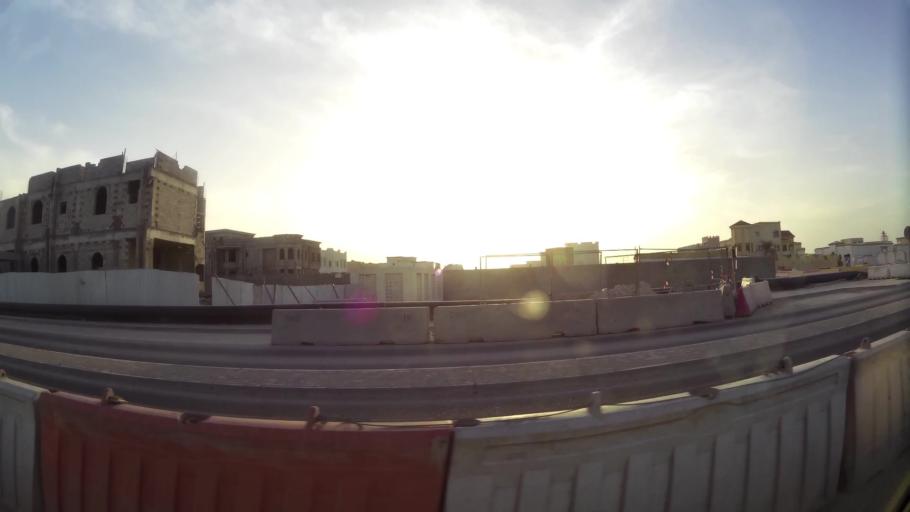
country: QA
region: Al Wakrah
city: Al Wakrah
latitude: 25.1575
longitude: 51.5921
